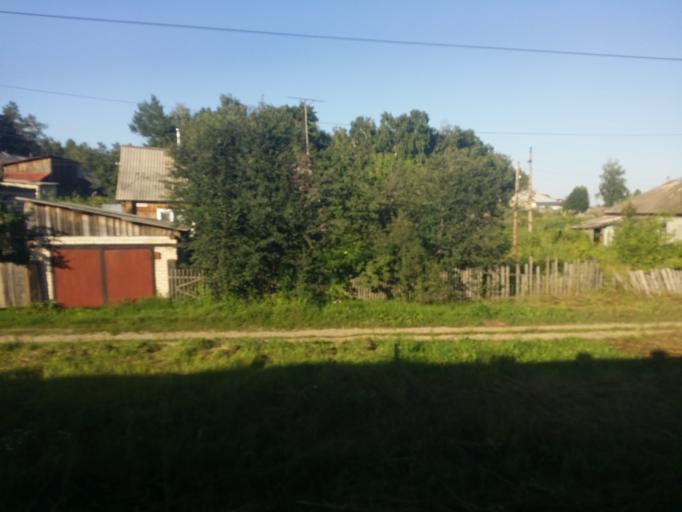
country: RU
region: Altai Krai
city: Troitskoye
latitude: 52.9854
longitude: 84.6600
